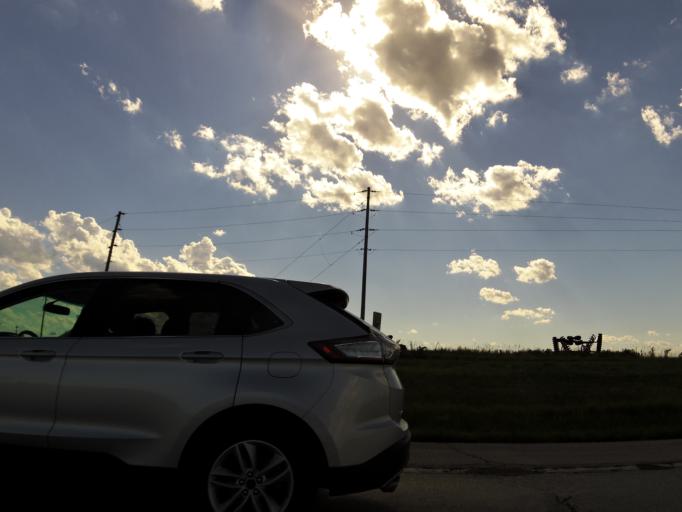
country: US
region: Missouri
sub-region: Marion County
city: Palmyra
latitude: 39.8817
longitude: -91.5251
